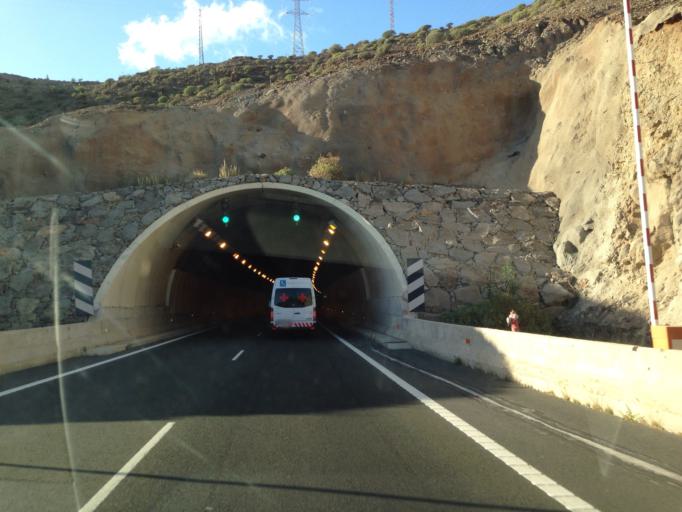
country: ES
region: Canary Islands
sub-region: Provincia de Las Palmas
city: Puerto Rico
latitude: 27.7885
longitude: -15.6923
